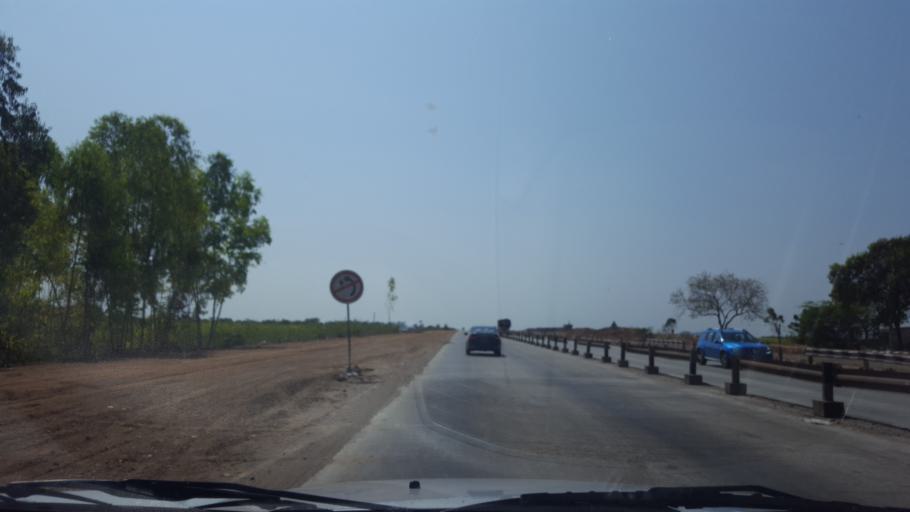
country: IN
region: Andhra Pradesh
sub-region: Prakasam
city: Addanki
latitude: 15.7877
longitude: 80.0376
